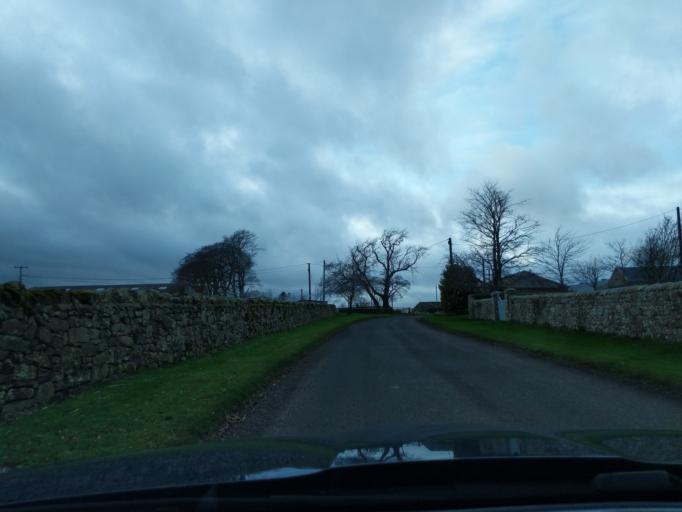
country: GB
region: England
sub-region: Northumberland
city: Ford
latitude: 55.7117
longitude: -2.0948
